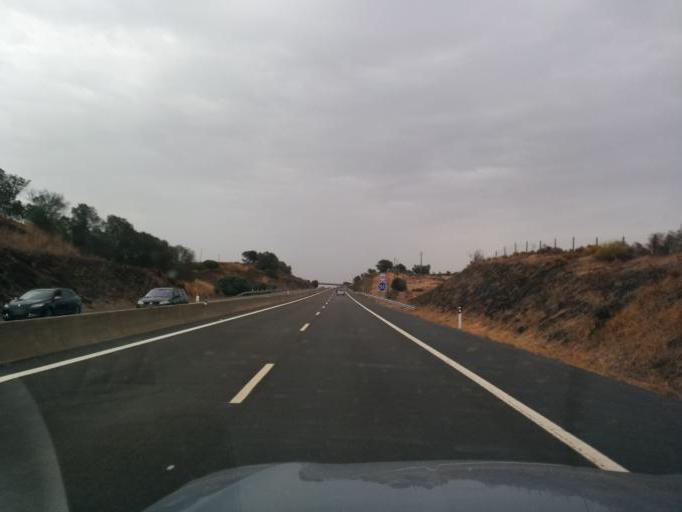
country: PT
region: Faro
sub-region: Vila Real de Santo Antonio
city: Monte Gordo
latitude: 37.1876
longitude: -7.5523
